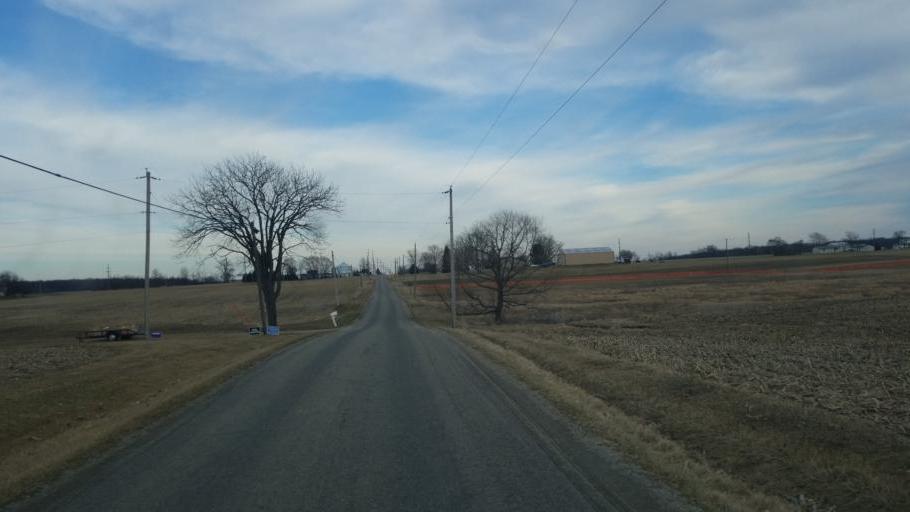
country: US
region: Ohio
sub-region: Defiance County
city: Hicksville
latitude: 41.3535
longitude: -84.7725
